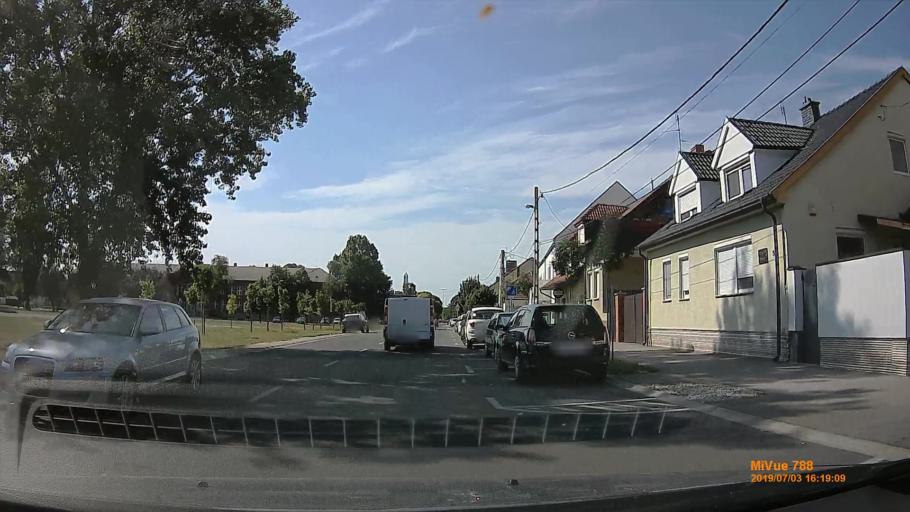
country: HU
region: Gyor-Moson-Sopron
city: Gyor
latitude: 47.6840
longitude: 17.6185
